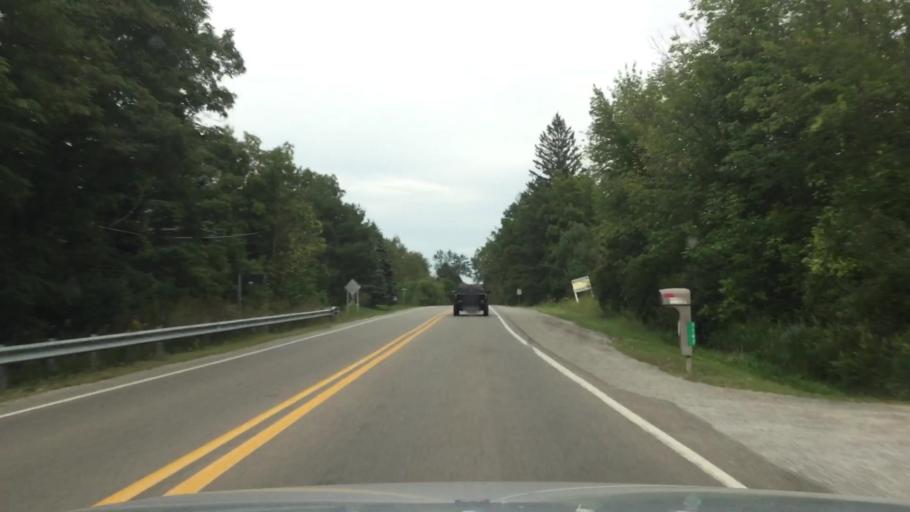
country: US
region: Michigan
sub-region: Genesee County
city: Lake Fenton
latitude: 42.8858
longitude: -83.6954
